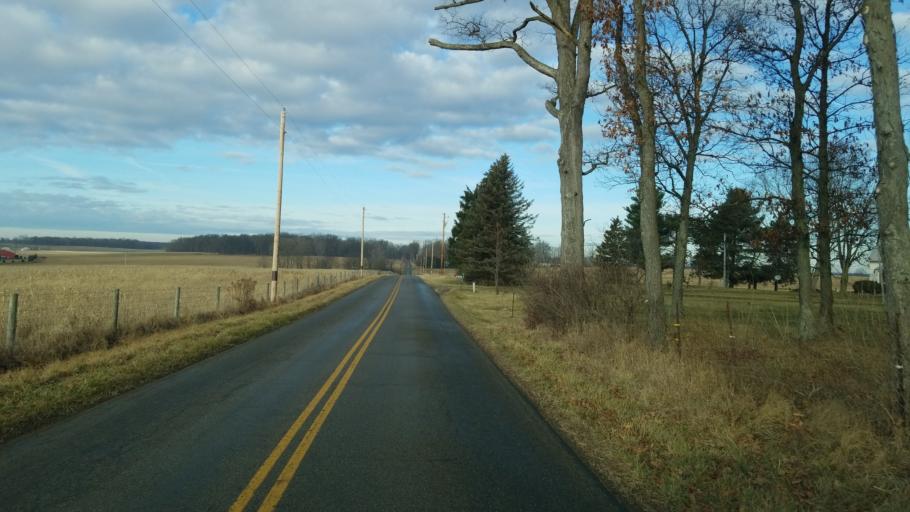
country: US
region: Ohio
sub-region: Knox County
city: Gambier
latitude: 40.3241
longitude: -82.3151
